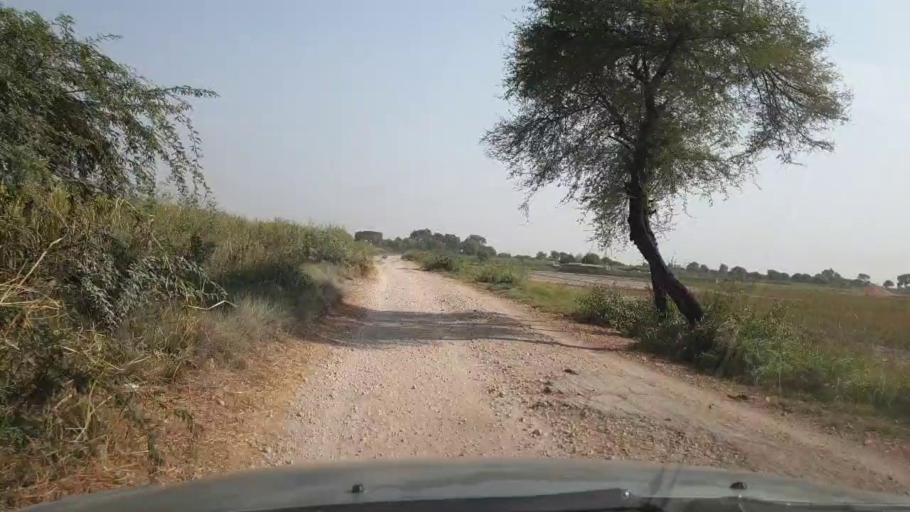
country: PK
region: Sindh
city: Bulri
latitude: 24.9084
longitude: 68.3715
